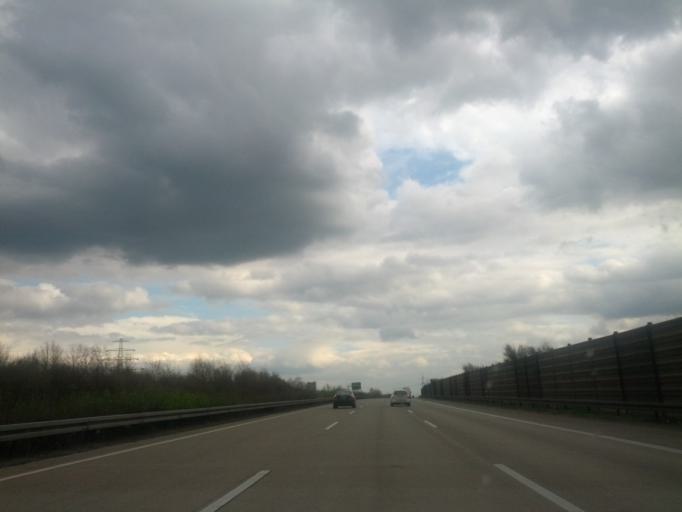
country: DE
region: Lower Saxony
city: Sarstedt
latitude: 52.2865
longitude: 9.9024
